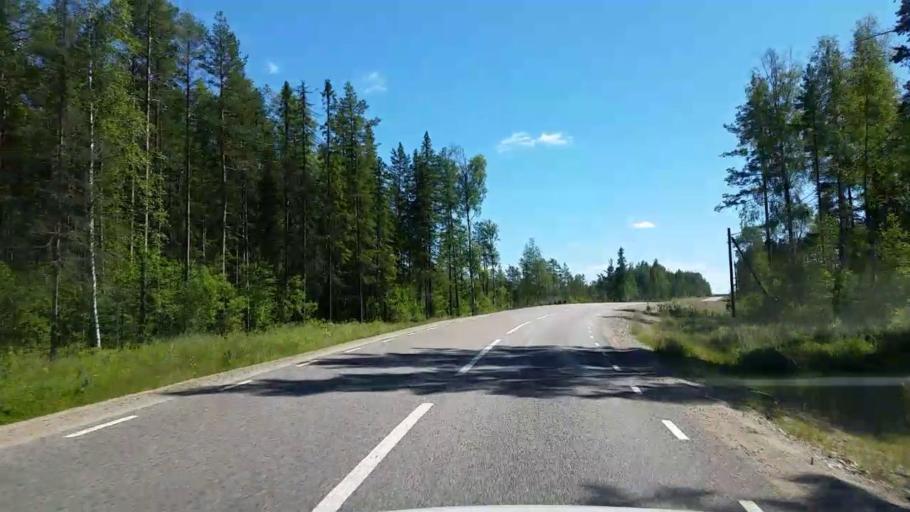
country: SE
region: Gaevleborg
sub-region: Ovanakers Kommun
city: Edsbyn
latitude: 61.4416
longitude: 15.7135
